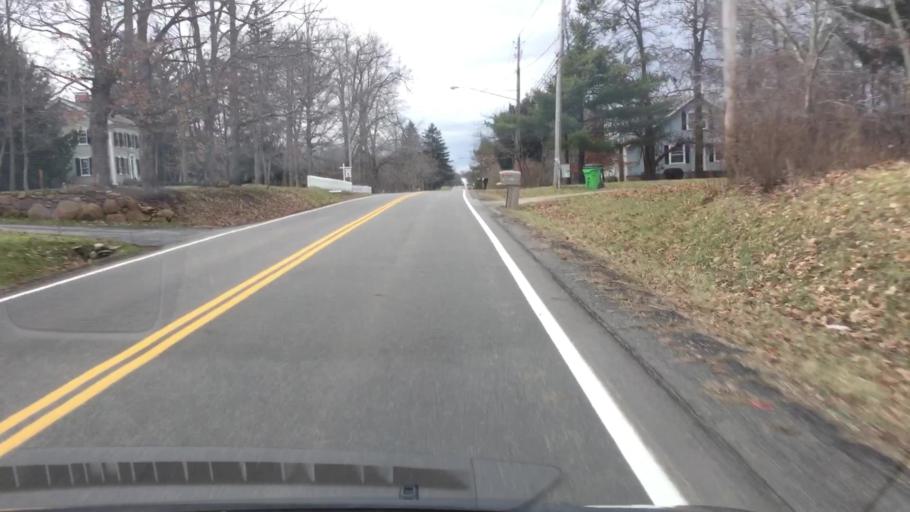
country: US
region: Ohio
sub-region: Summit County
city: Boston Heights
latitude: 41.2425
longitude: -81.5004
